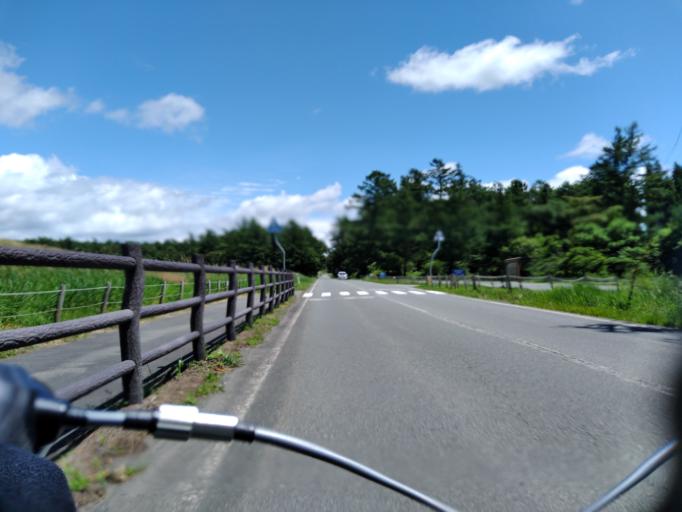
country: JP
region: Iwate
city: Shizukuishi
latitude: 39.7550
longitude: 141.0044
